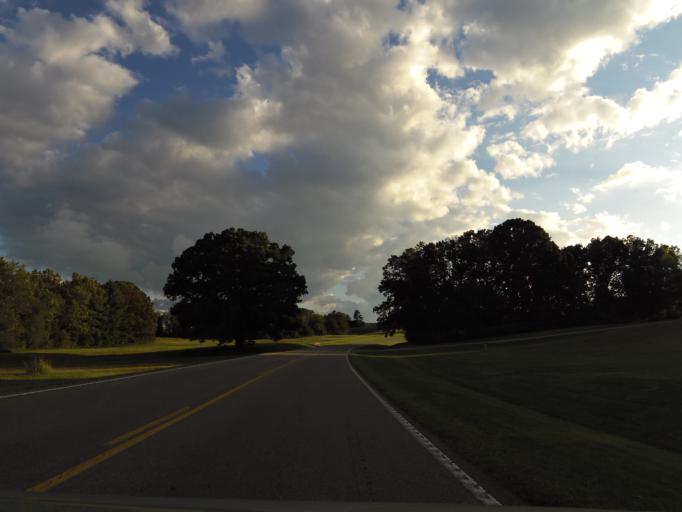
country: US
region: Tennessee
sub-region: Jefferson County
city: Jefferson City
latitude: 36.1612
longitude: -83.5078
